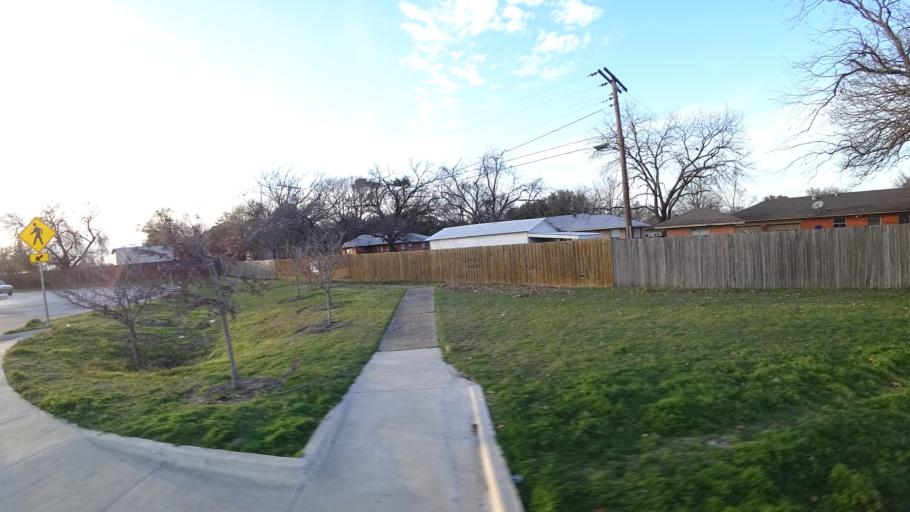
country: US
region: Texas
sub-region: Denton County
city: Lewisville
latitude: 33.0395
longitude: -97.0005
